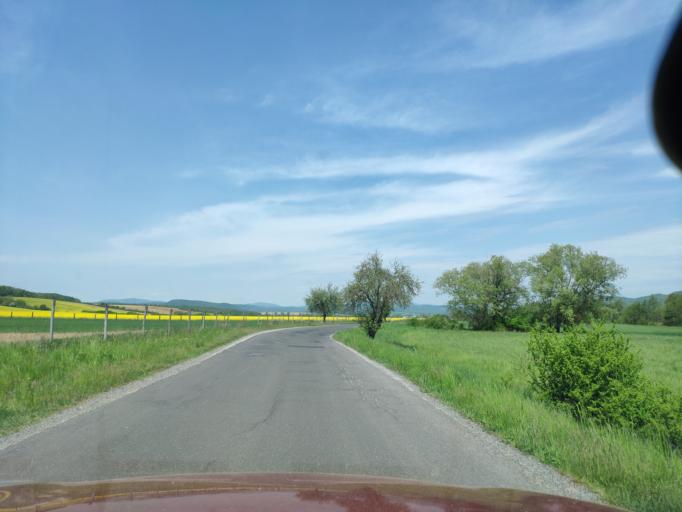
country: SK
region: Banskobystricky
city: Rimavska Sobota
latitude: 48.4268
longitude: 20.1175
